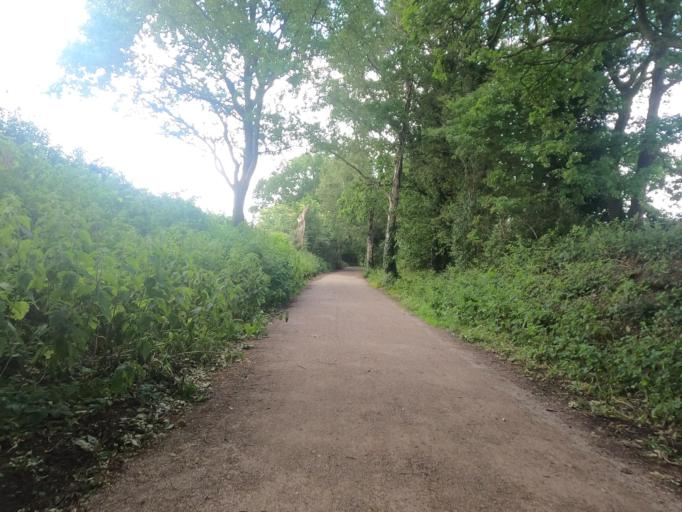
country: GB
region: England
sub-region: Cheshire West and Chester
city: Over
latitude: 53.2056
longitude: -2.5712
